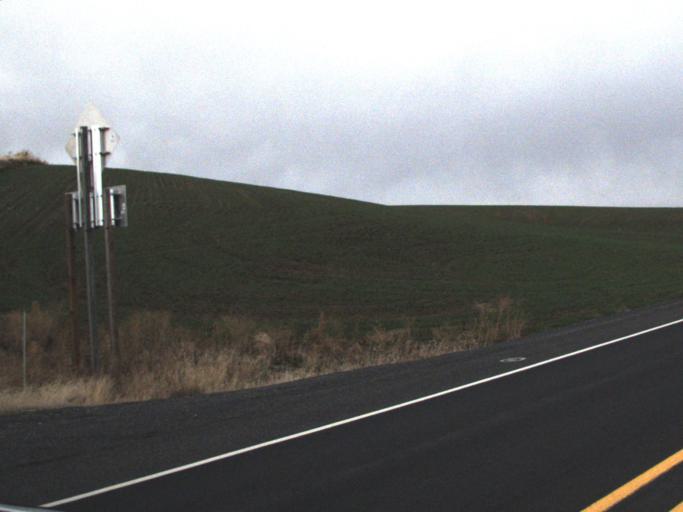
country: US
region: Washington
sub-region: Whitman County
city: Colfax
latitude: 46.8111
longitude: -117.6584
